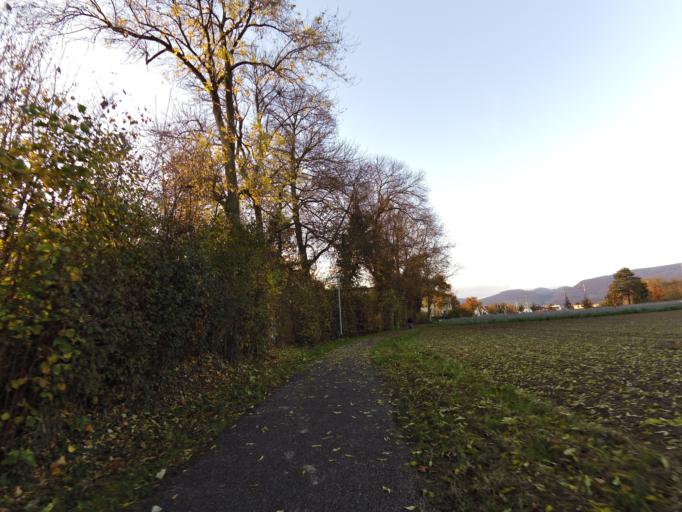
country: CH
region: Aargau
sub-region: Bezirk Aarau
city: Suhr
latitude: 47.3801
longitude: 8.0811
